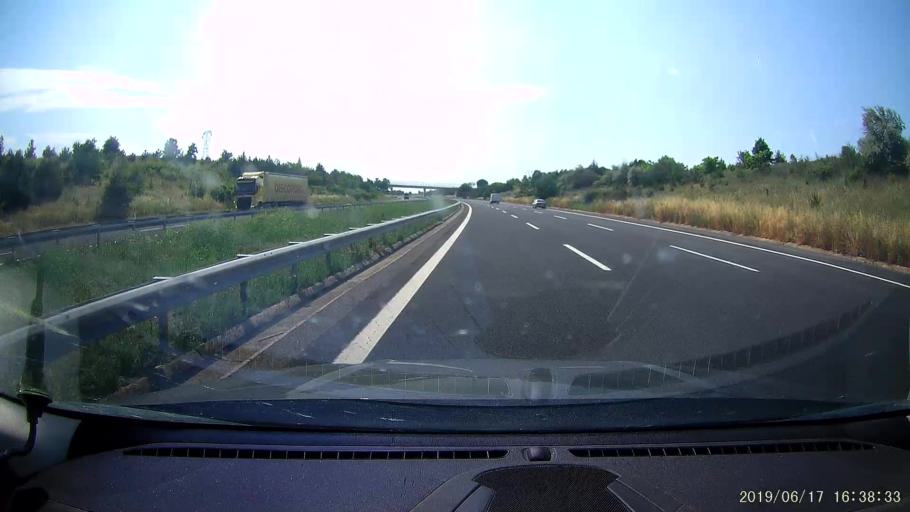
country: TR
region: Kirklareli
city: Luleburgaz
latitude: 41.4469
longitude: 27.4394
